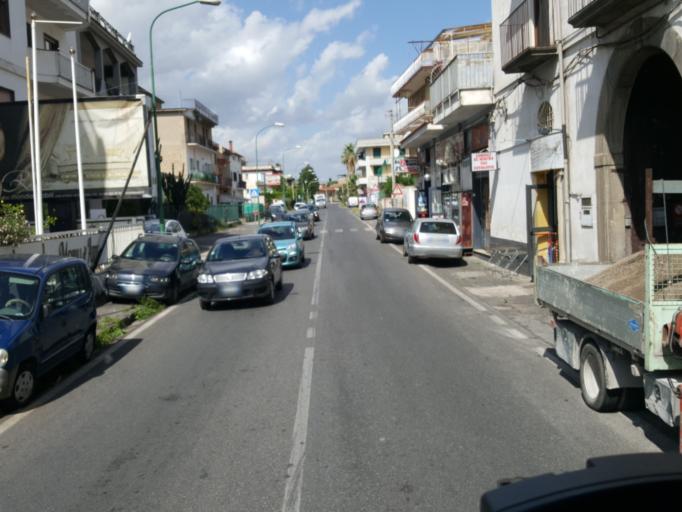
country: IT
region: Campania
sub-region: Provincia di Napoli
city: Liveri
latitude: 40.9031
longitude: 14.5654
